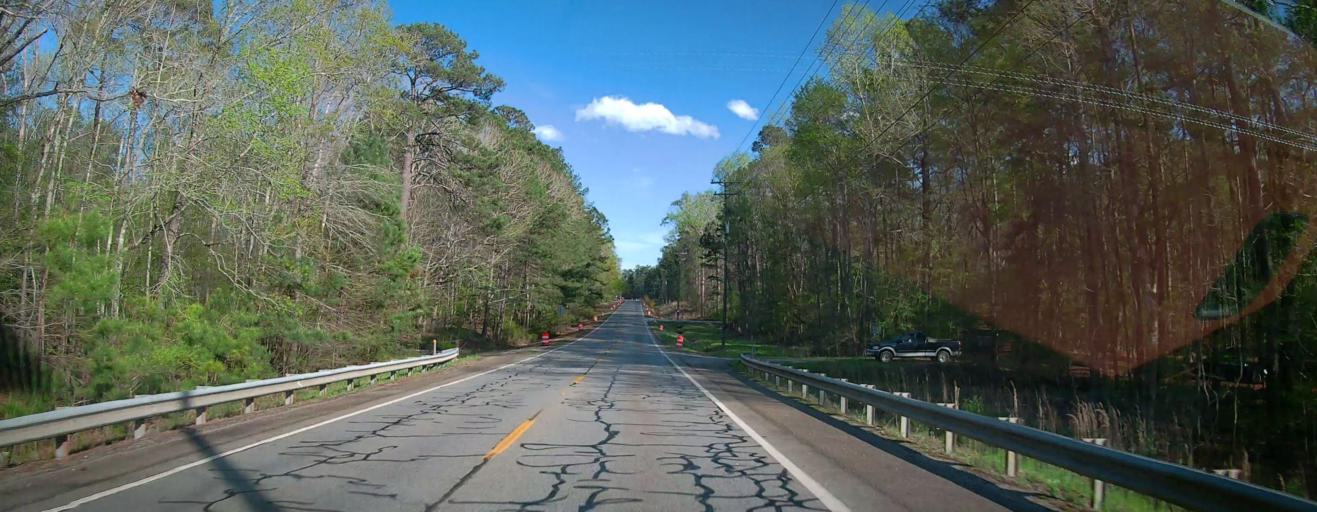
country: US
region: Georgia
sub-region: Baldwin County
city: Milledgeville
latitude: 33.1628
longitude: -83.3740
